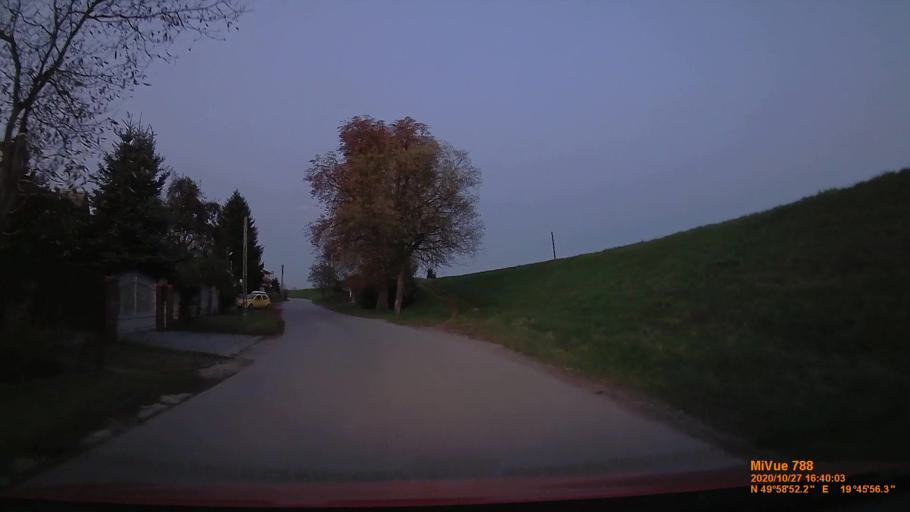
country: PL
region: Lesser Poland Voivodeship
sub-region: Powiat krakowski
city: Raczna
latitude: 49.9812
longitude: 19.7658
